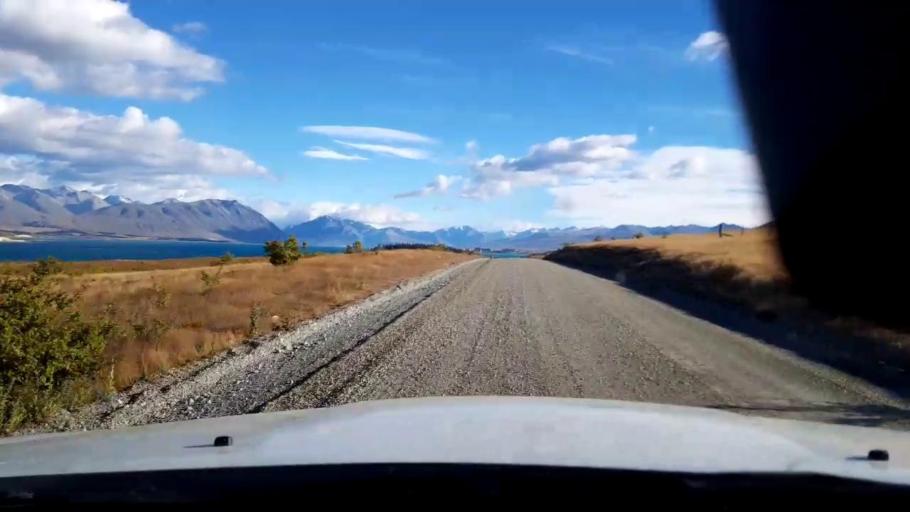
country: NZ
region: Canterbury
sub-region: Timaru District
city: Pleasant Point
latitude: -43.9730
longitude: 170.5127
